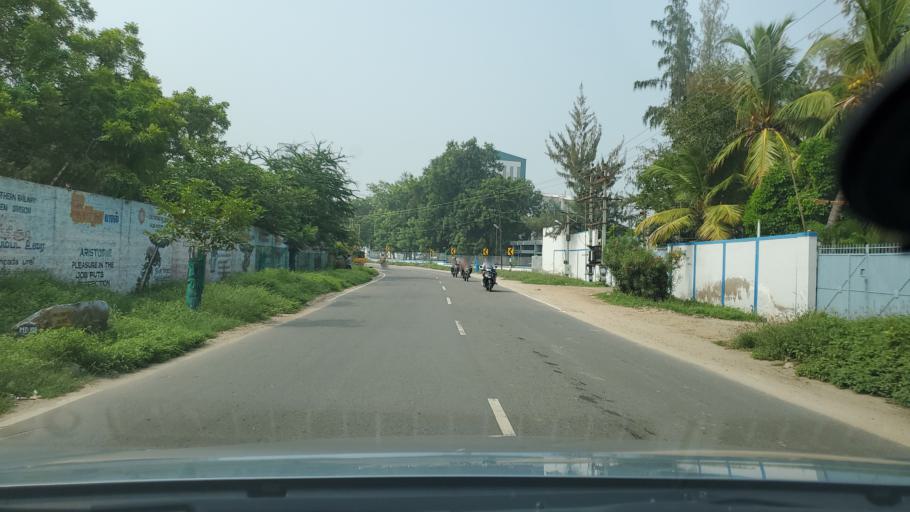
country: IN
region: Tamil Nadu
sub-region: Erode
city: Erode
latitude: 11.3231
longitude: 77.7151
